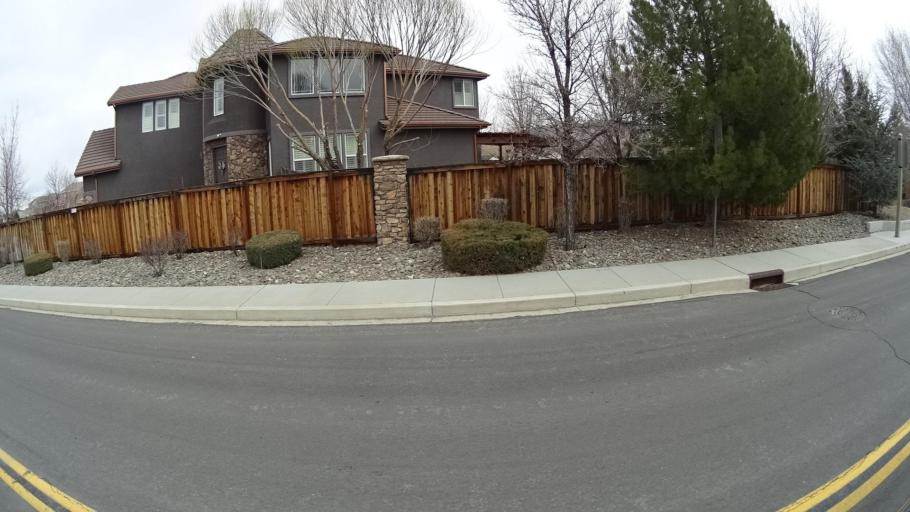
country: US
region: Nevada
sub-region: Washoe County
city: Spanish Springs
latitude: 39.6254
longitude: -119.6866
